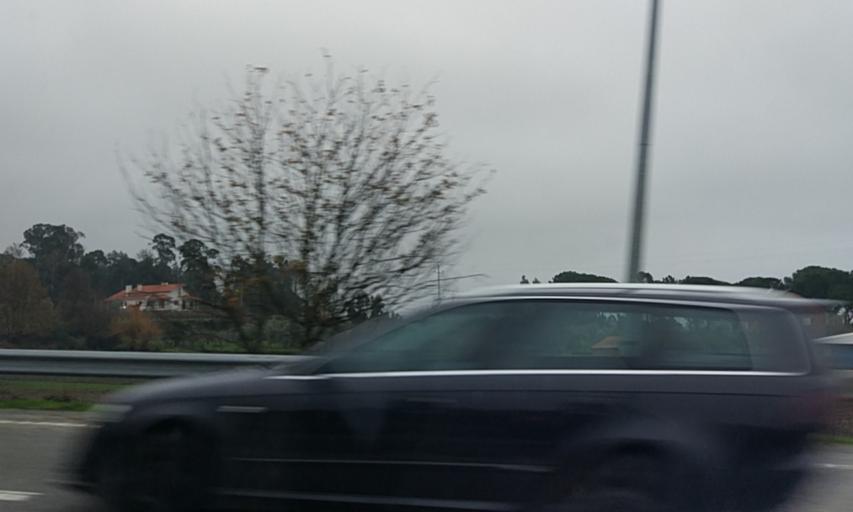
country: PT
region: Viseu
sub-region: Concelho de Tondela
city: Tondela
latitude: 40.5381
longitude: -8.0560
